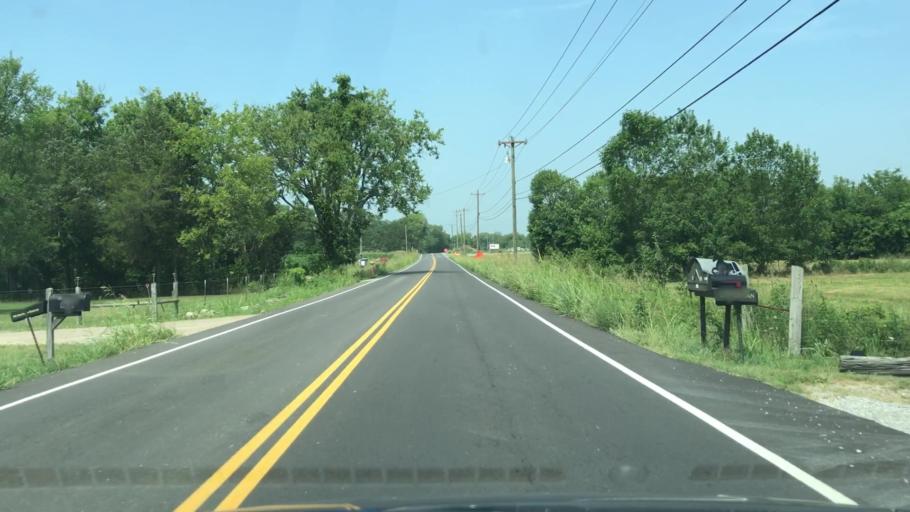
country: US
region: Tennessee
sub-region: Wilson County
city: Rural Hill
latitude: 36.1131
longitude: -86.4256
